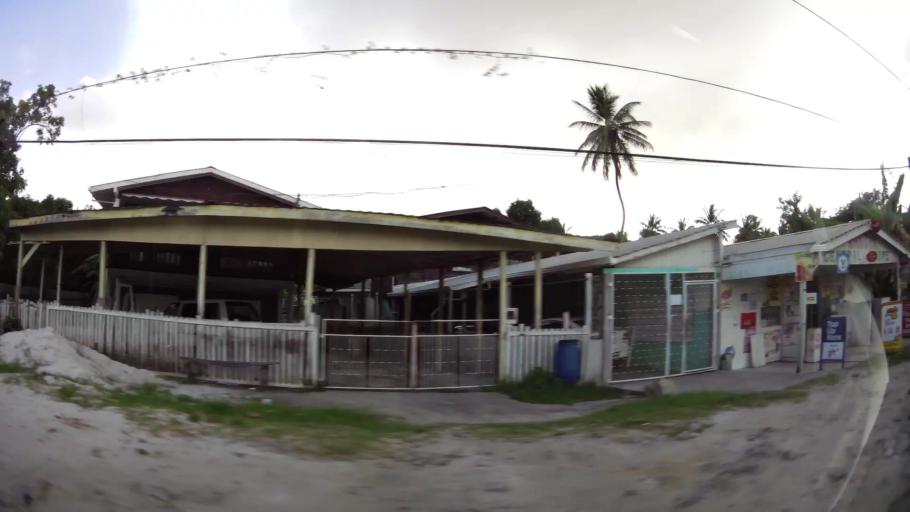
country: GY
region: Demerara-Mahaica
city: Georgetown
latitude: 6.7881
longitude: -58.0176
